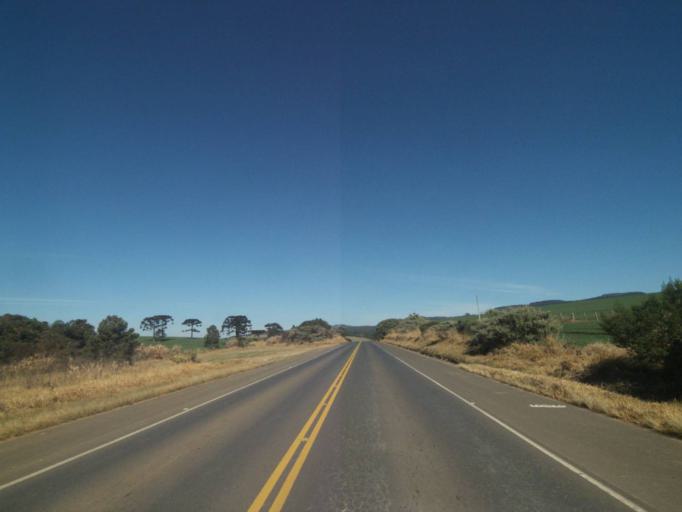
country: BR
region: Parana
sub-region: Tibagi
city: Tibagi
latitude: -24.5419
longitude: -50.4479
